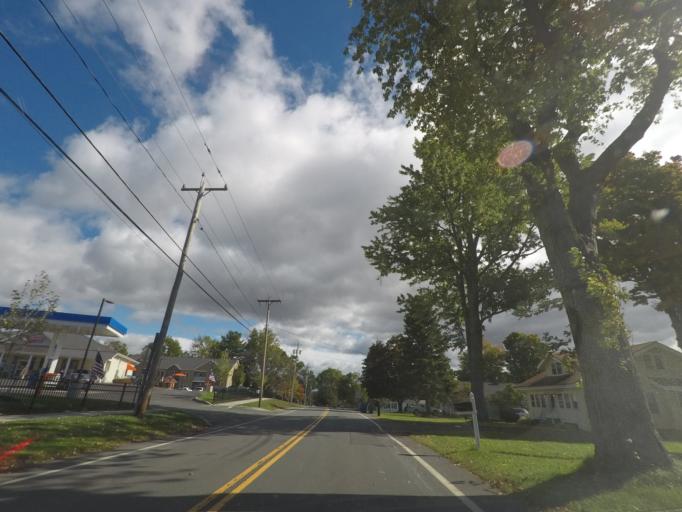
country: US
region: New York
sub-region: Albany County
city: Cohoes
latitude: 42.7833
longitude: -73.7436
